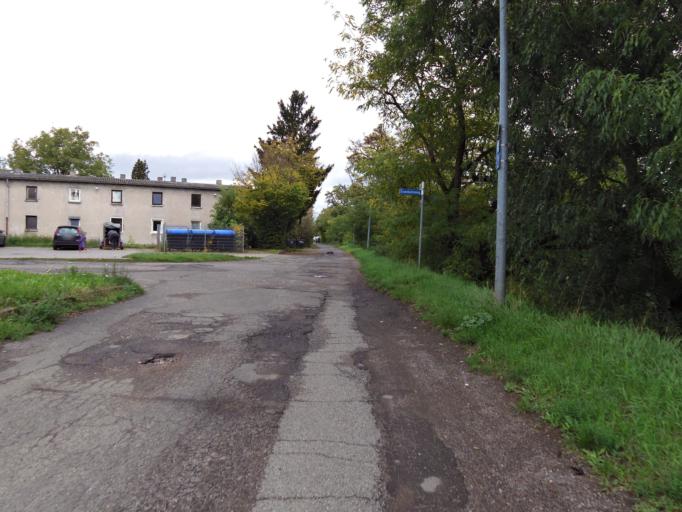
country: DE
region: Rheinland-Pfalz
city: Worms
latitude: 49.6474
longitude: 8.3578
